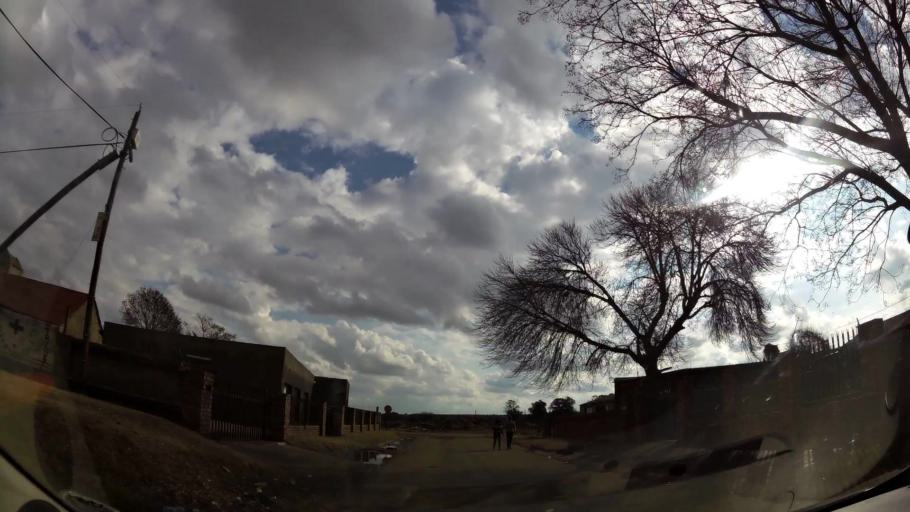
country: ZA
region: Orange Free State
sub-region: Fezile Dabi District Municipality
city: Sasolburg
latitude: -26.8423
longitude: 27.8413
